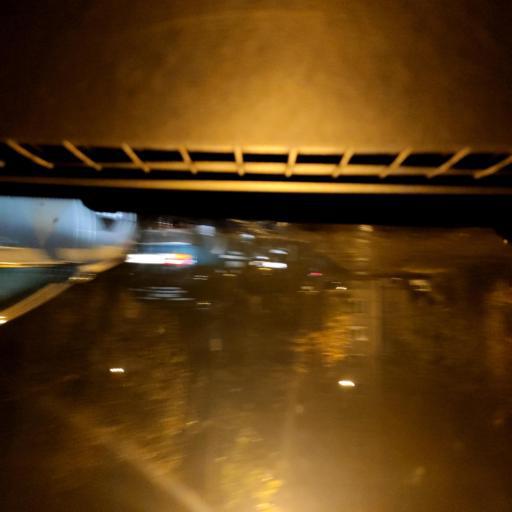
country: RU
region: Voronezj
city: Podgornoye
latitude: 51.7218
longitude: 39.1734
